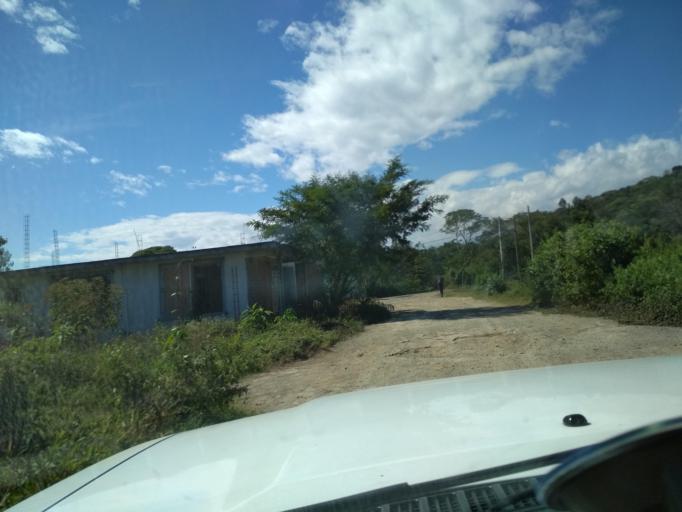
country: MX
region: Veracruz
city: El Castillo
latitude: 19.5526
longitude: -96.8563
